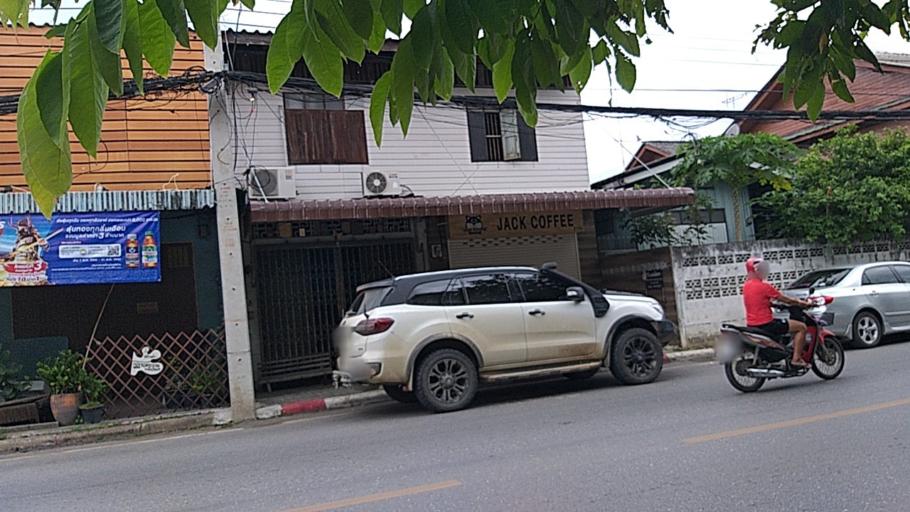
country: TH
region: Nakhon Pathom
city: Nakhon Pathom
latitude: 13.8222
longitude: 100.0501
